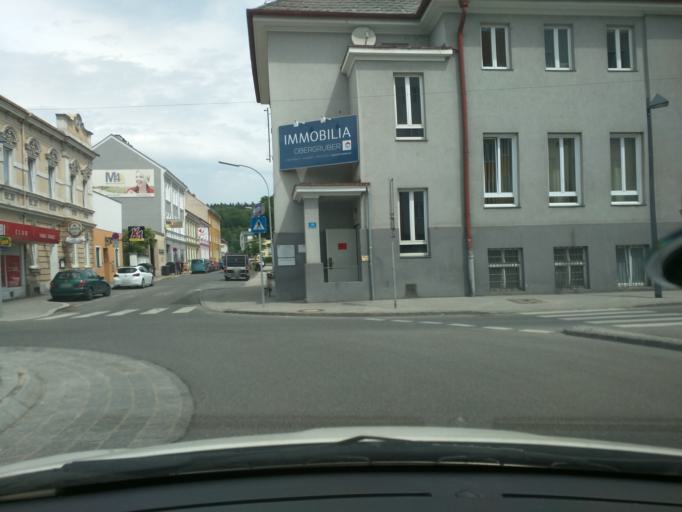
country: AT
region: Lower Austria
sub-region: Politischer Bezirk Amstetten
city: Amstetten
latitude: 48.1229
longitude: 14.8801
